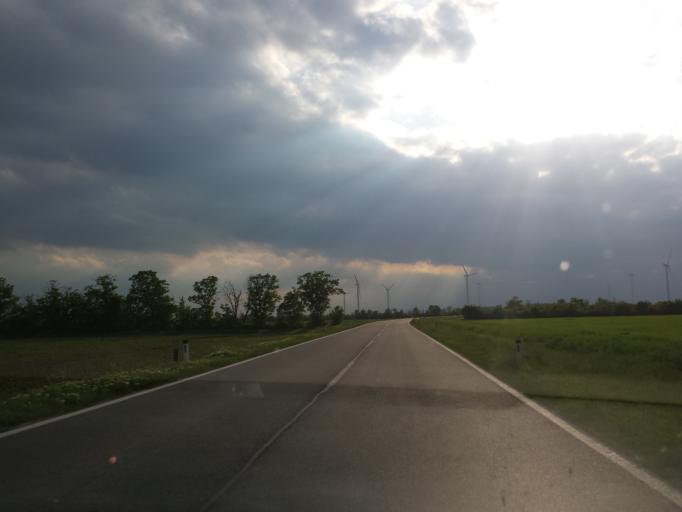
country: AT
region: Lower Austria
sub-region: Politischer Bezirk Ganserndorf
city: Obersiebenbrunn
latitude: 48.2612
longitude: 16.6949
